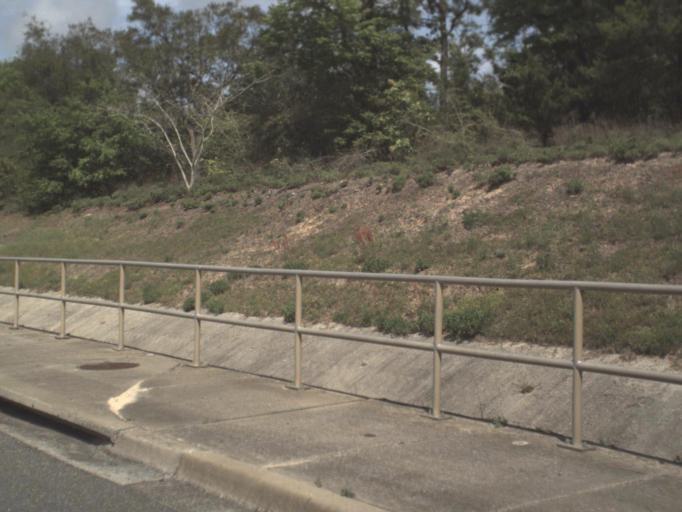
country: US
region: Florida
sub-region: Santa Rosa County
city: Holley
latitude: 30.4449
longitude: -86.8720
